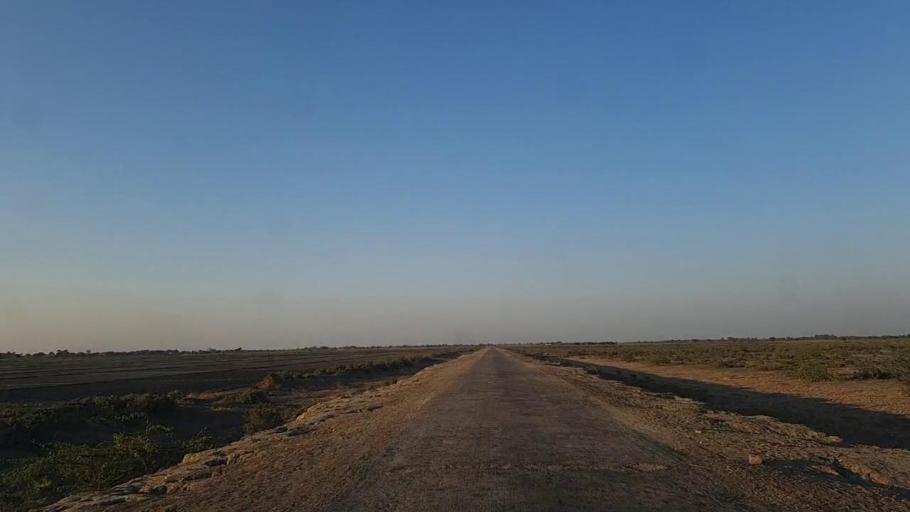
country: PK
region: Sindh
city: Naukot
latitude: 25.0108
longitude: 69.4167
